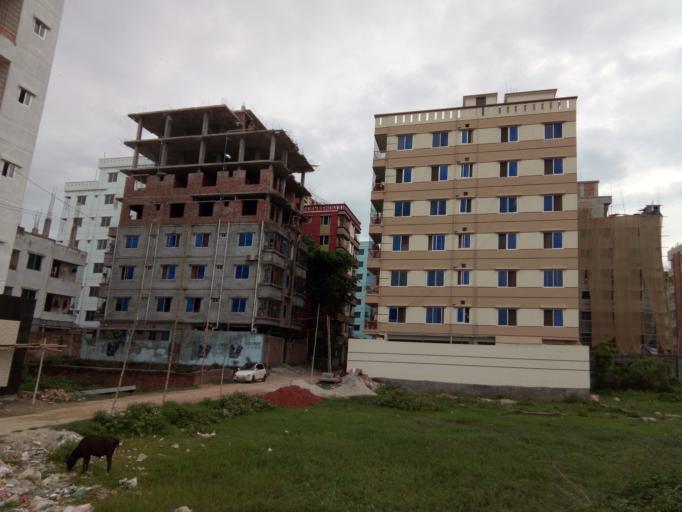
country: BD
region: Dhaka
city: Paltan
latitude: 23.7603
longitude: 90.4458
